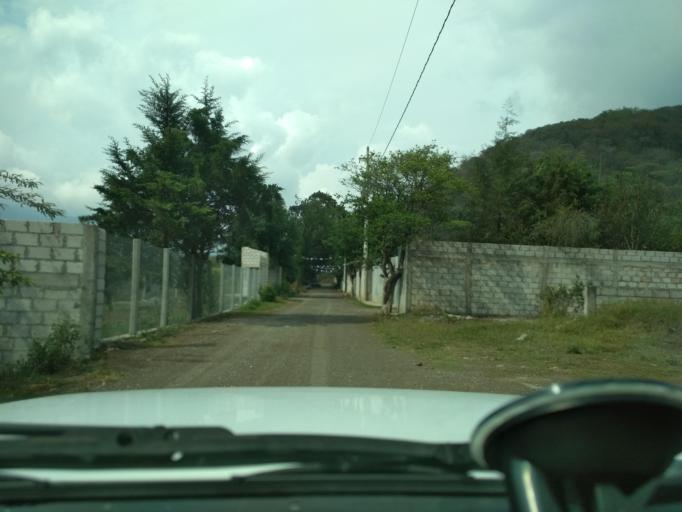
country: MX
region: Veracruz
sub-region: Nogales
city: Taza de Agua Ojo Zarco
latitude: 18.7803
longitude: -97.2015
